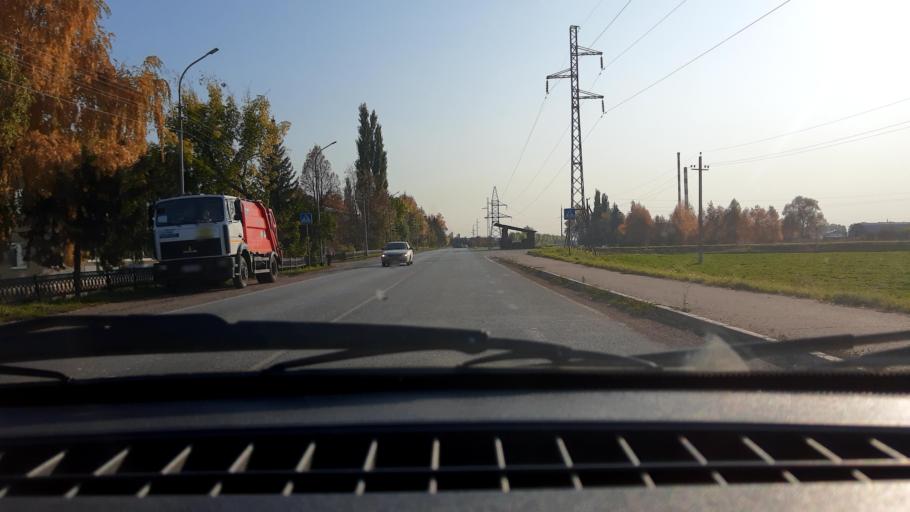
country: RU
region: Bashkortostan
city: Ufa
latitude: 54.8312
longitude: 55.9947
